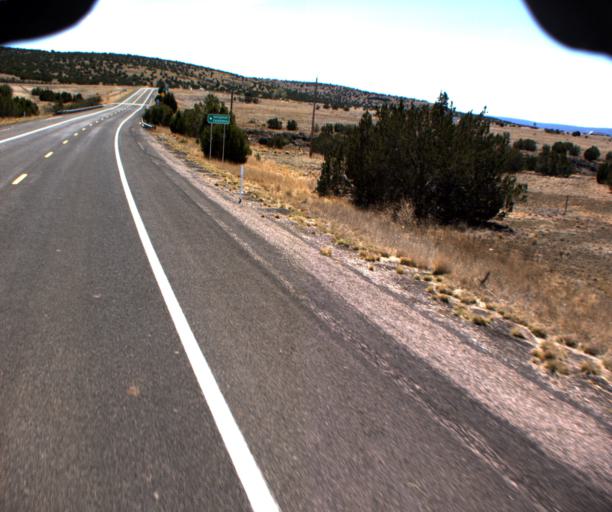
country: US
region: Arizona
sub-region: Mohave County
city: Peach Springs
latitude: 35.3248
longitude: -112.8911
